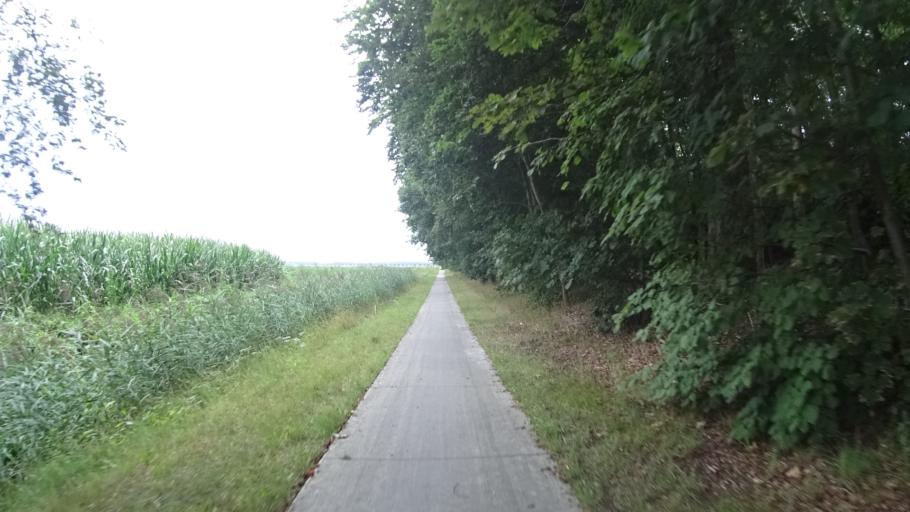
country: NL
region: Groningen
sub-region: Gemeente Slochteren
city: Slochteren
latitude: 53.2120
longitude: 6.8221
